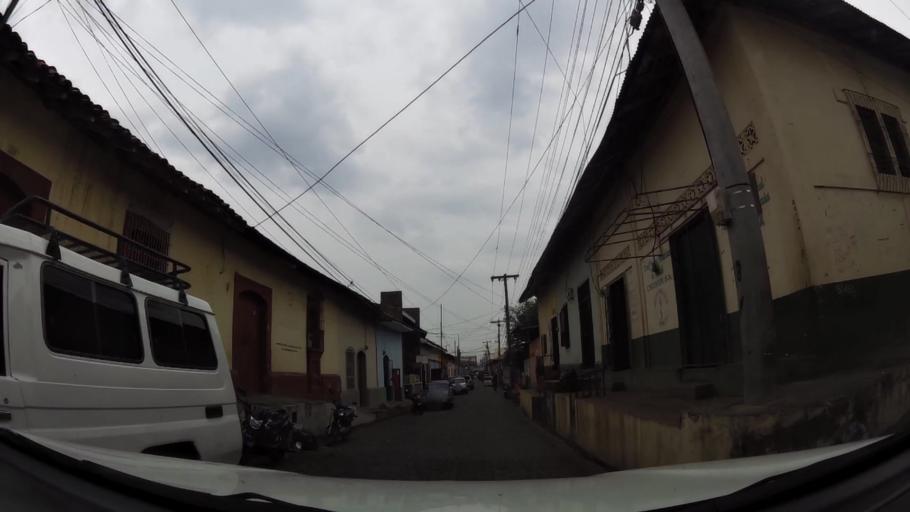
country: NI
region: Leon
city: Leon
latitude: 12.4351
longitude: -86.8739
